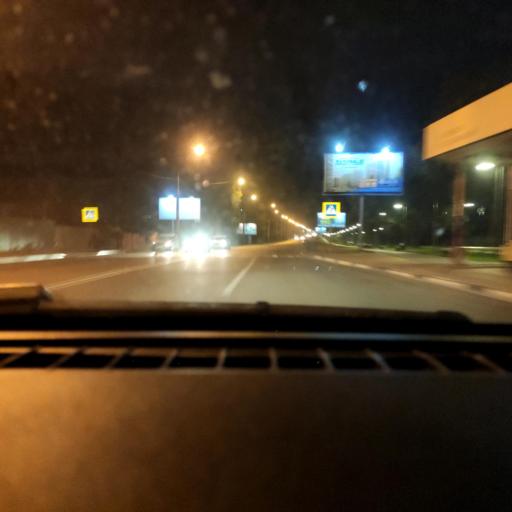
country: RU
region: Voronezj
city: Voronezh
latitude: 51.6655
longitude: 39.2683
